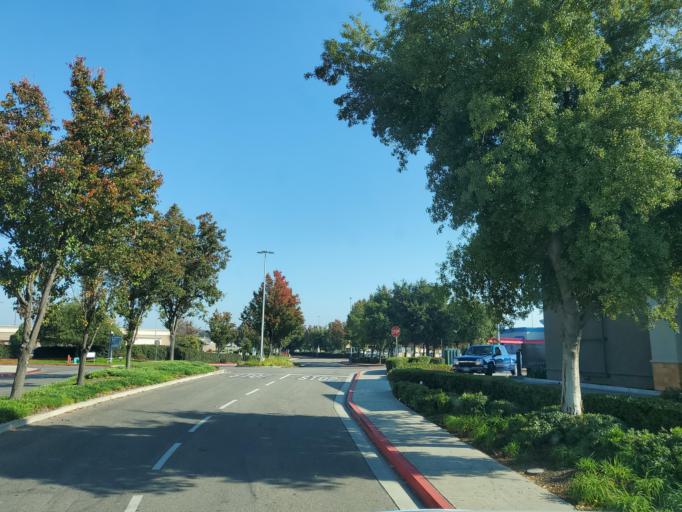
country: US
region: California
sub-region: San Joaquin County
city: Lincoln Village
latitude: 38.0509
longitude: -121.3748
